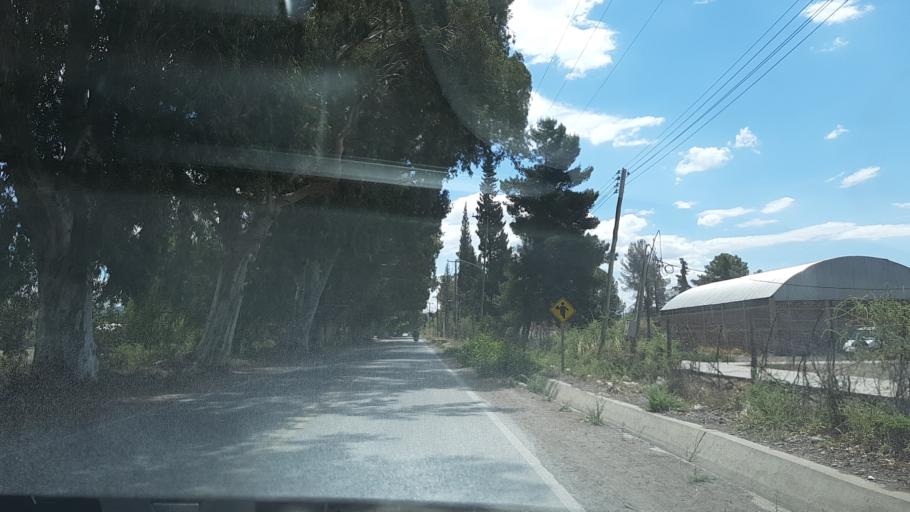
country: AR
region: San Juan
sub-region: Departamento de Rivadavia
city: Rivadavia
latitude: -31.5557
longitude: -68.6101
